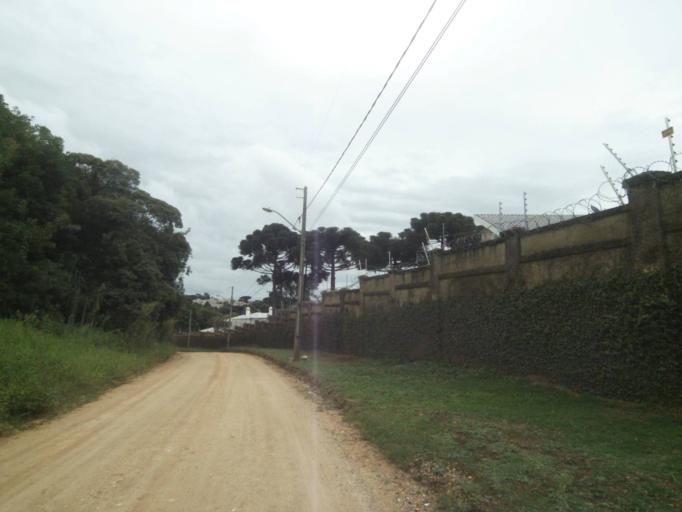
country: BR
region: Parana
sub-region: Curitiba
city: Curitiba
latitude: -25.4564
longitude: -49.3382
